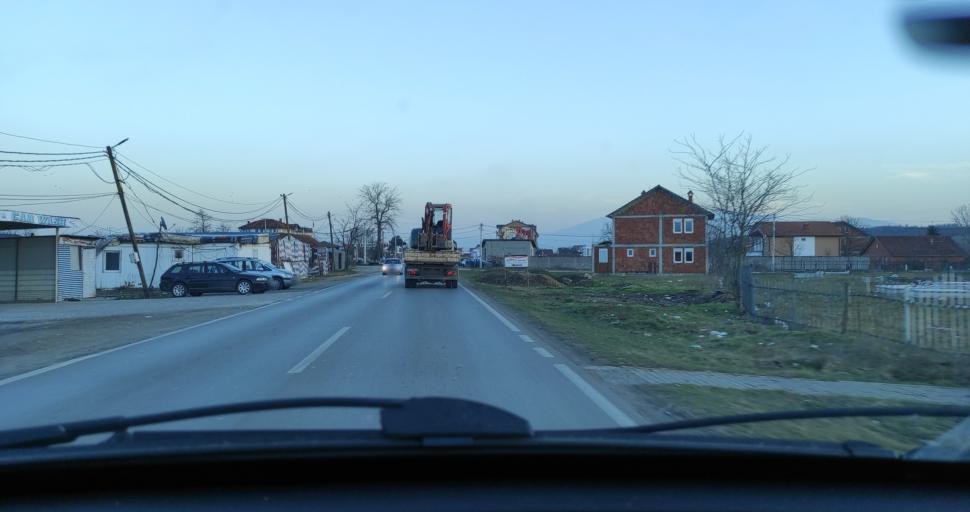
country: XK
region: Gjakova
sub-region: Komuna e Gjakoves
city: Gjakove
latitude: 42.4121
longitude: 20.4018
